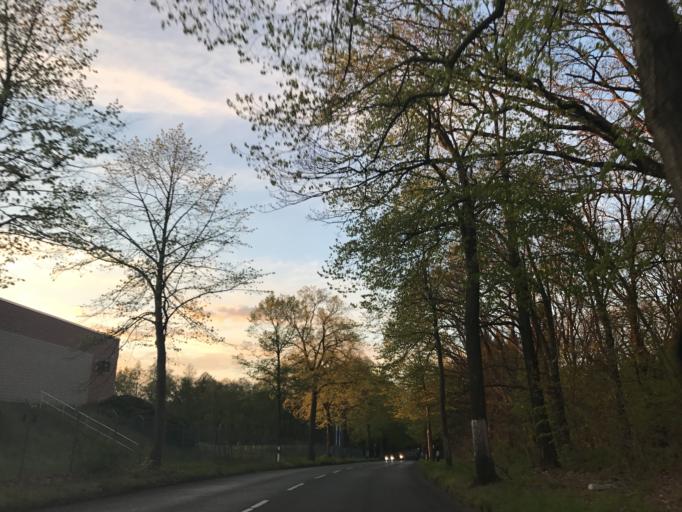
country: DE
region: Berlin
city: Haselhorst
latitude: 52.5165
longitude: 13.2187
